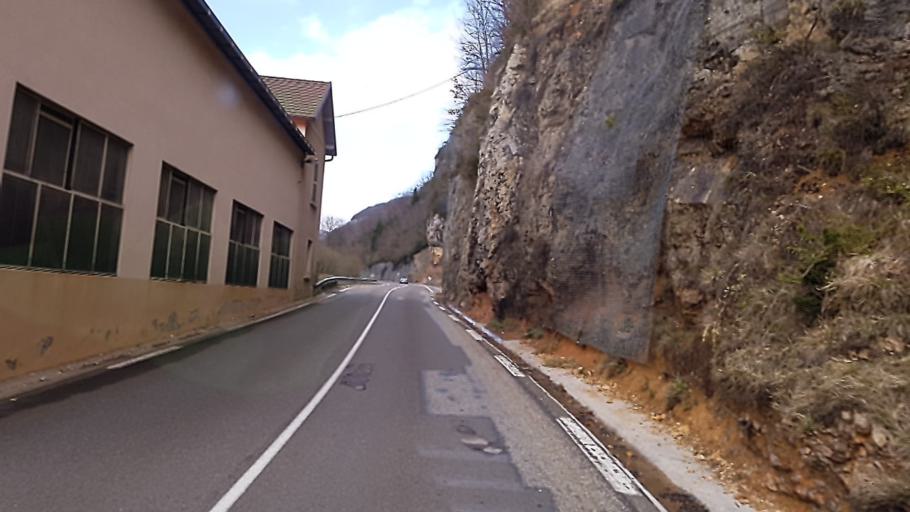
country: FR
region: Franche-Comte
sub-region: Departement du Jura
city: Lavans-les-Saint-Claude
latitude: 46.3662
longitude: 5.8029
